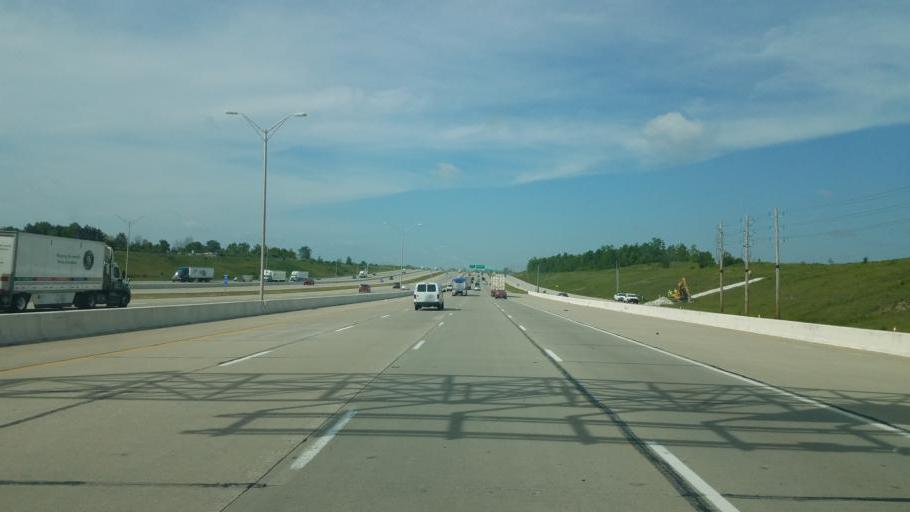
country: US
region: Indiana
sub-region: Marion County
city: Speedway
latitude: 39.7044
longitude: -86.2892
